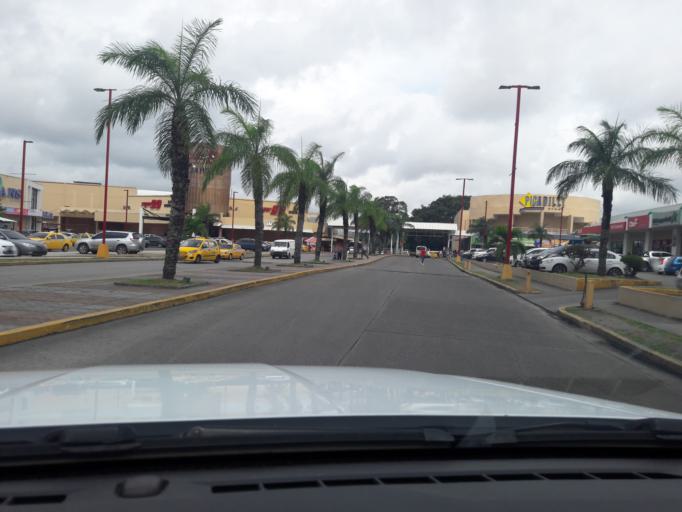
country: PA
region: Panama
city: San Miguelito
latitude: 9.0483
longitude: -79.5071
